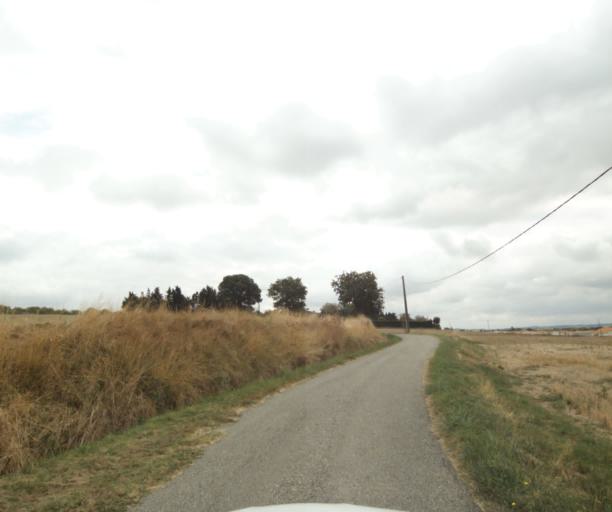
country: FR
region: Midi-Pyrenees
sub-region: Departement de la Haute-Garonne
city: Villefranche-de-Lauragais
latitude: 43.4159
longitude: 1.7121
